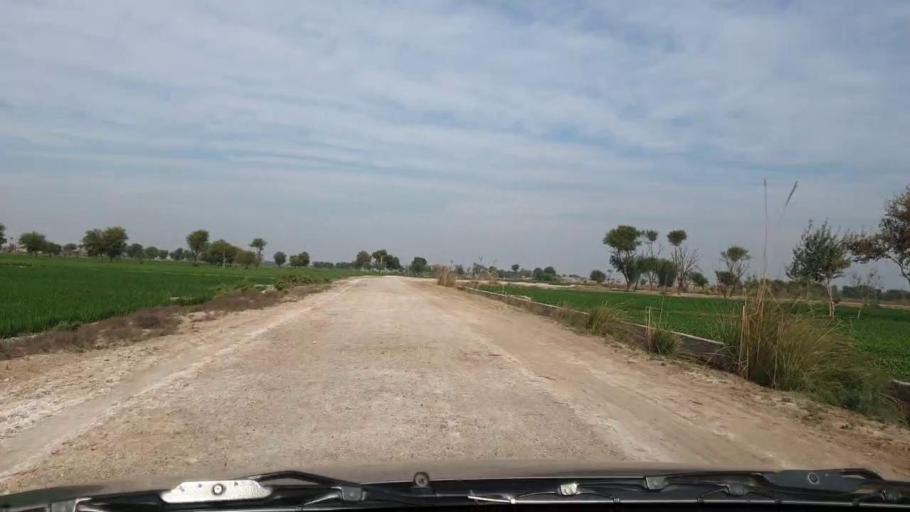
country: PK
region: Sindh
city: Jam Sahib
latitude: 26.2910
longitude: 68.6928
